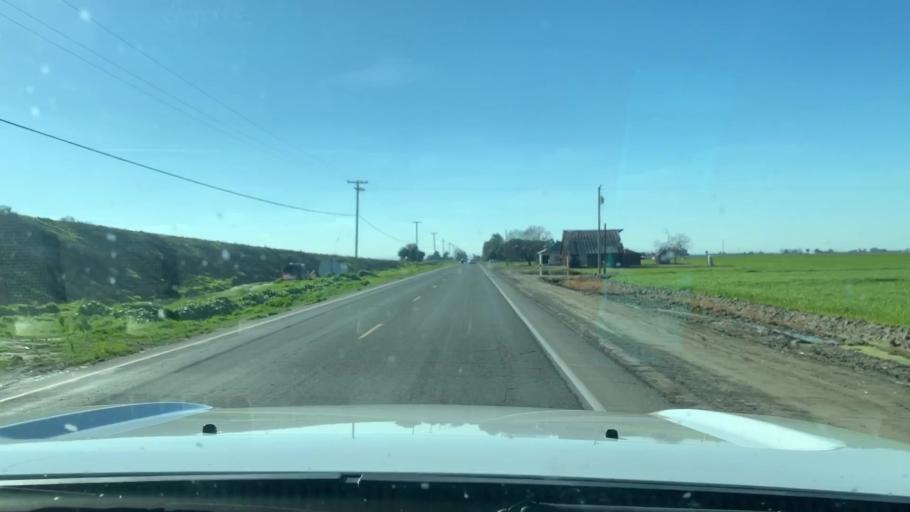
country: US
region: California
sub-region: Kings County
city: Home Garden
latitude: 36.2111
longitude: -119.6133
